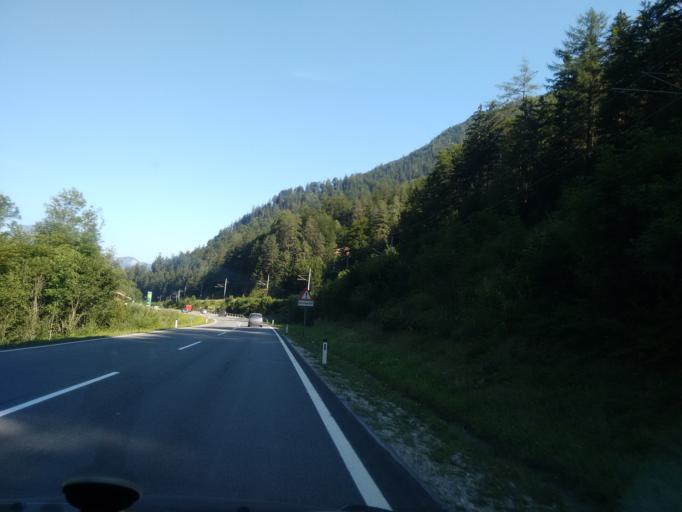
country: AT
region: Styria
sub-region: Politischer Bezirk Liezen
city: Bad Aussee
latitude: 47.5853
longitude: 13.8028
